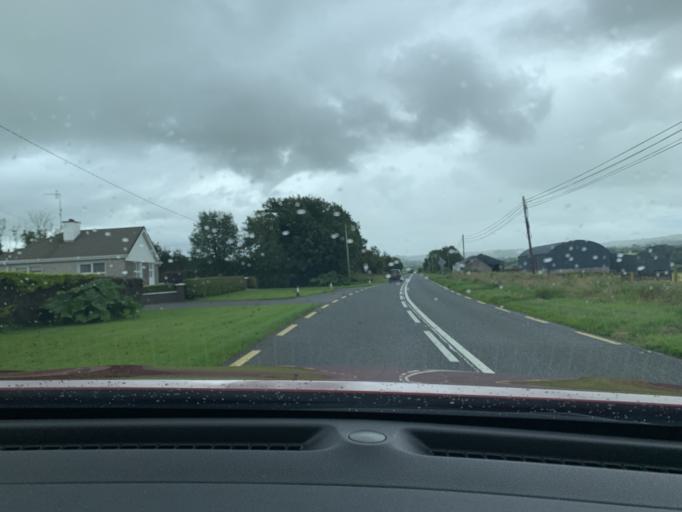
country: IE
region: Ulster
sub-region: County Donegal
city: Raphoe
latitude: 54.7977
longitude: -7.5662
